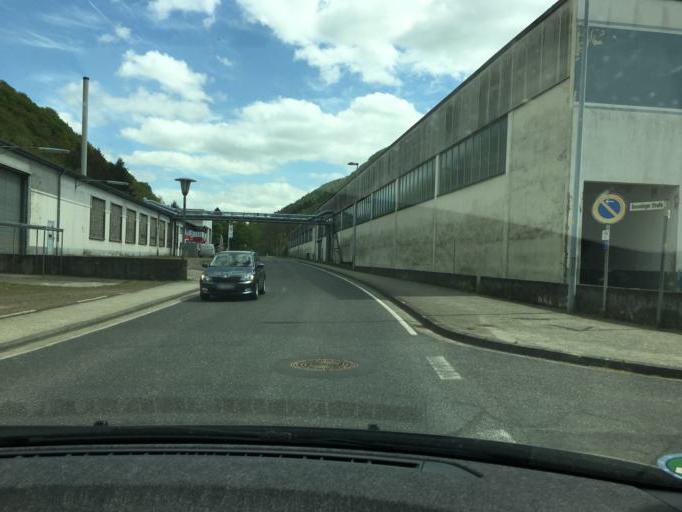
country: DE
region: Rheinland-Pfalz
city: Ahrbruck
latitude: 50.4833
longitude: 6.9870
